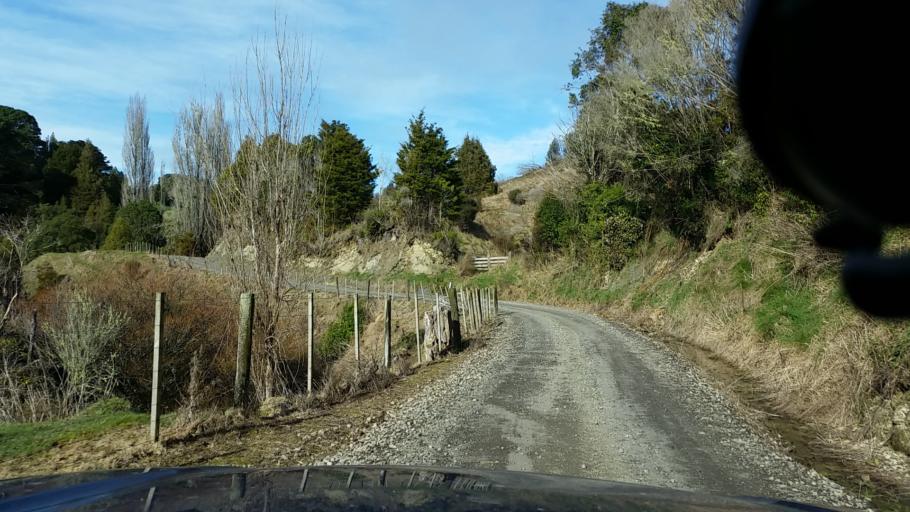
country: NZ
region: Taranaki
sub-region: New Plymouth District
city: Waitara
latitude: -39.0334
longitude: 174.7783
